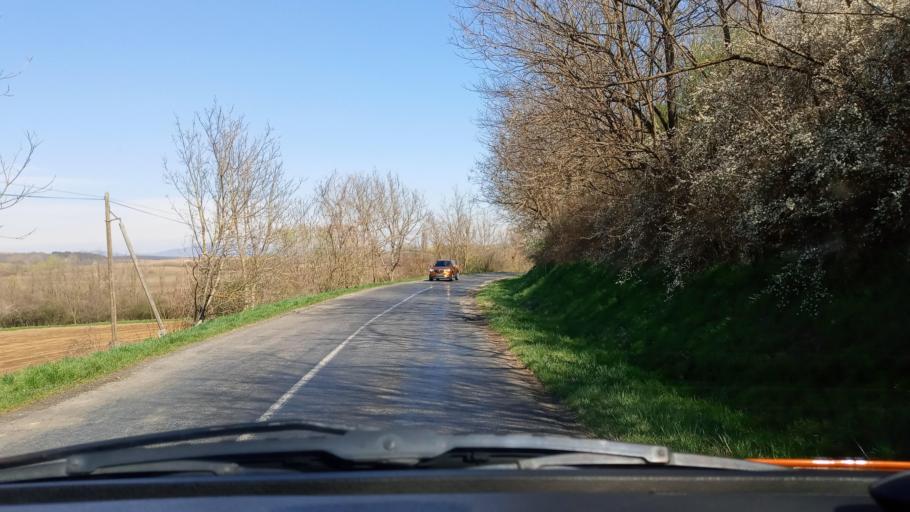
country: HU
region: Baranya
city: Boly
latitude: 46.0181
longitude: 18.4557
